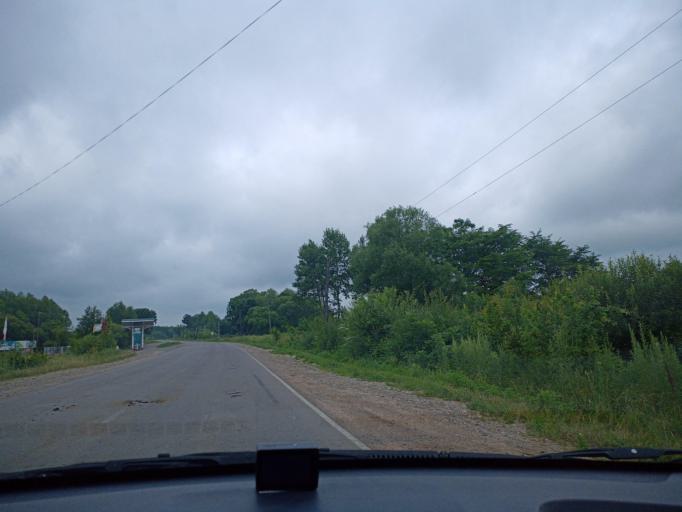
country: RU
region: Primorskiy
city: Novopokrovka
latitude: 45.8918
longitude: 134.8528
